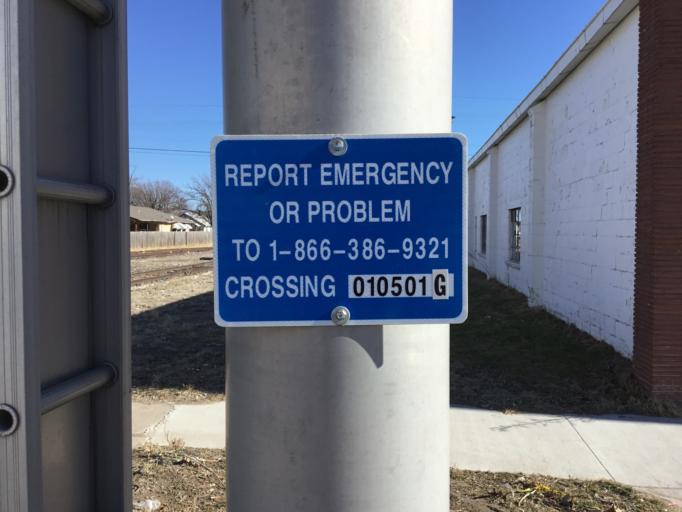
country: US
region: Kansas
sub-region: McPherson County
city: McPherson
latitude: 38.3724
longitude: -97.6655
